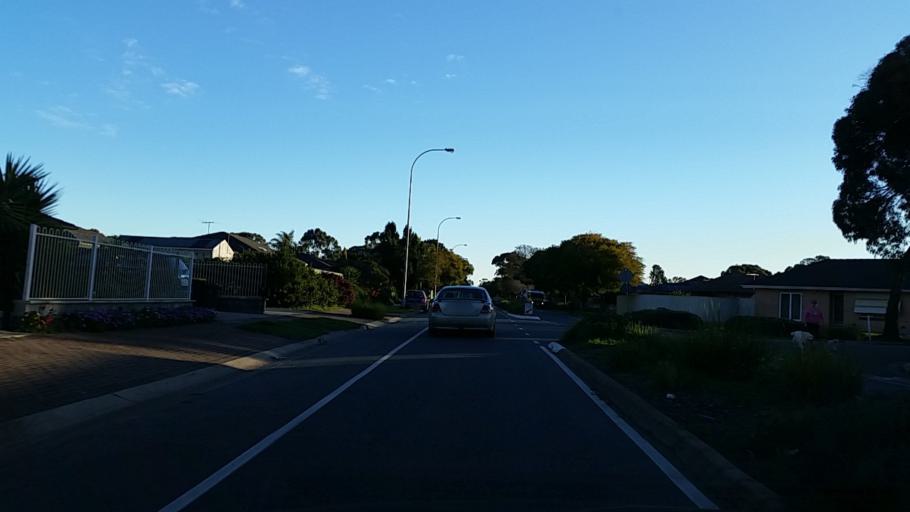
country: AU
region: South Australia
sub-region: Salisbury
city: Salisbury
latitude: -34.7486
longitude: 138.6377
